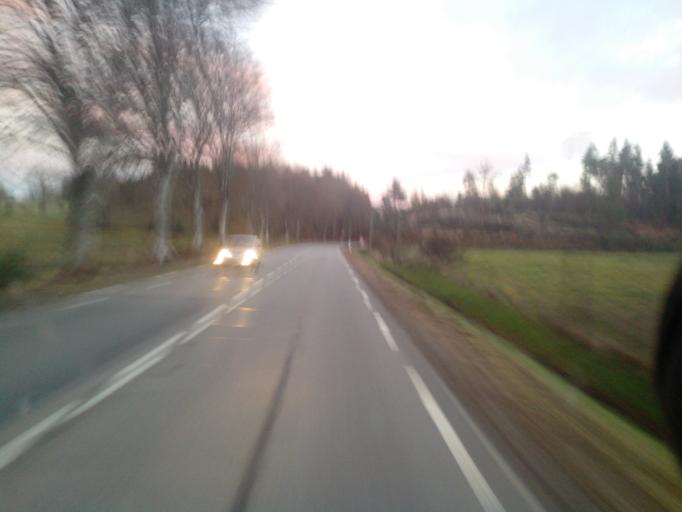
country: FR
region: Limousin
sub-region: Departement de la Correze
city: Meymac
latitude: 45.5136
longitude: 2.1836
